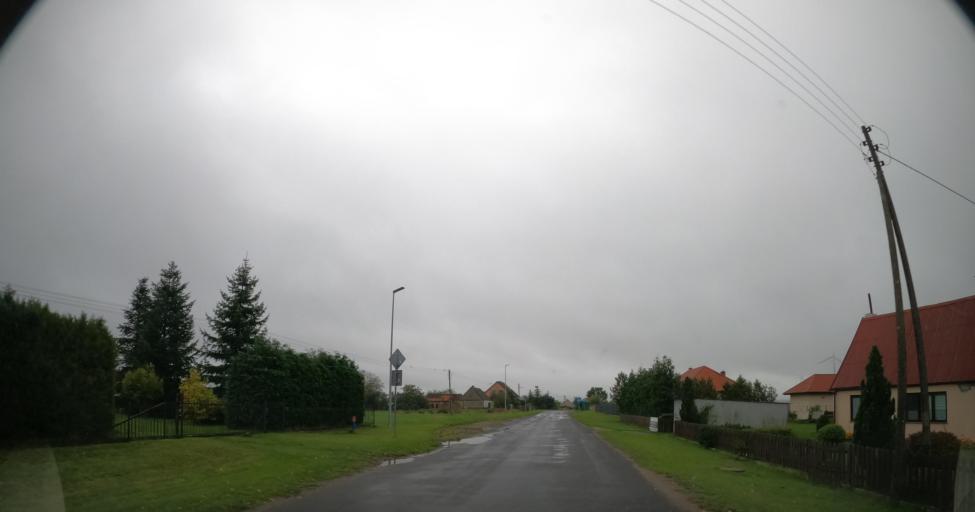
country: PL
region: West Pomeranian Voivodeship
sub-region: Powiat pyrzycki
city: Kozielice
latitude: 53.0708
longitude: 14.7871
